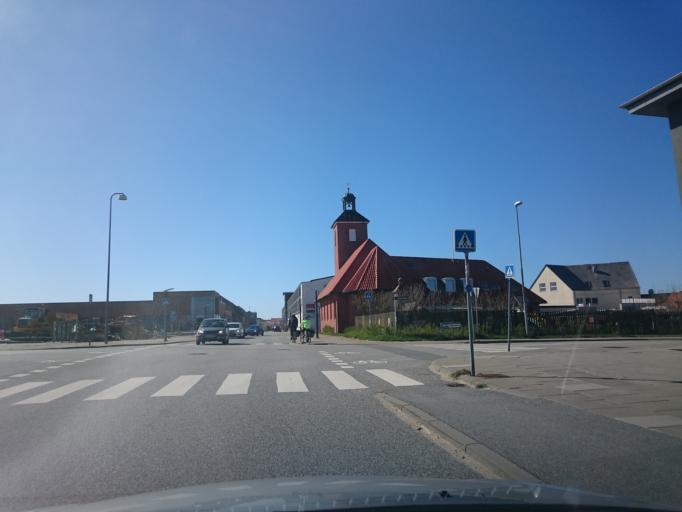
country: DK
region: North Denmark
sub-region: Hjorring Kommune
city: Hirtshals
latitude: 57.5905
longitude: 9.9622
